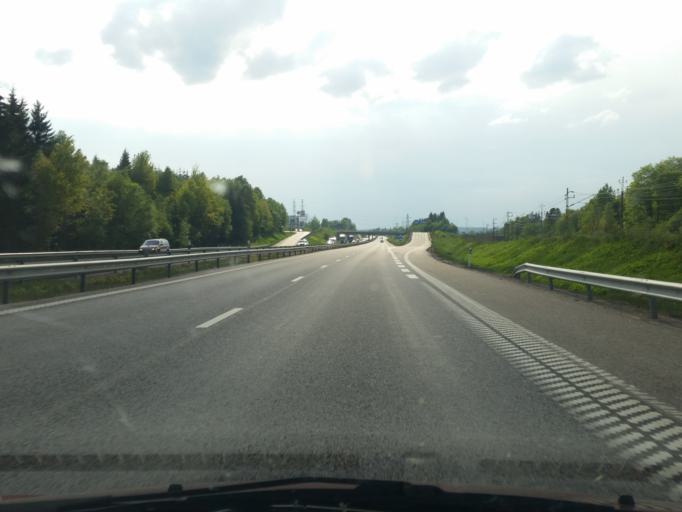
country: SE
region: Vaestra Goetaland
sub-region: Boras Kommun
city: Sjomarken
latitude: 57.7117
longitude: 12.8794
